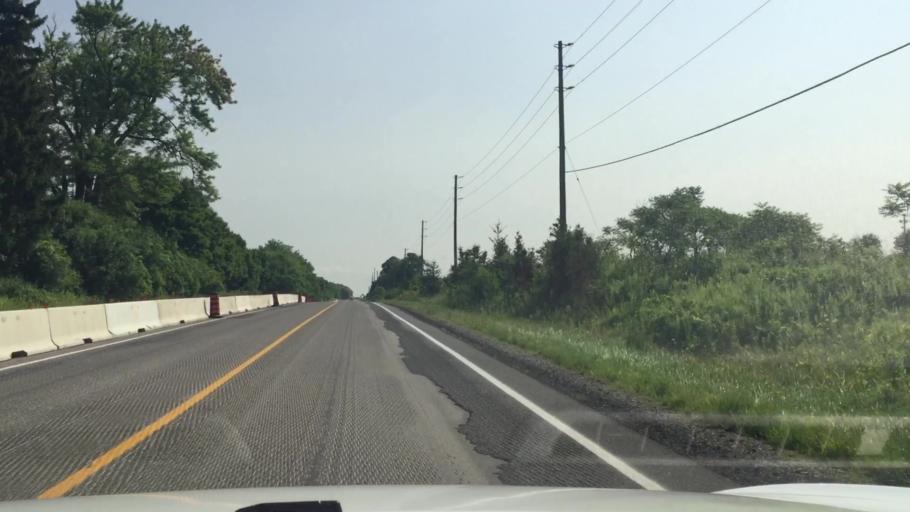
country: CA
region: Ontario
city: Pickering
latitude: 43.9106
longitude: -79.1426
